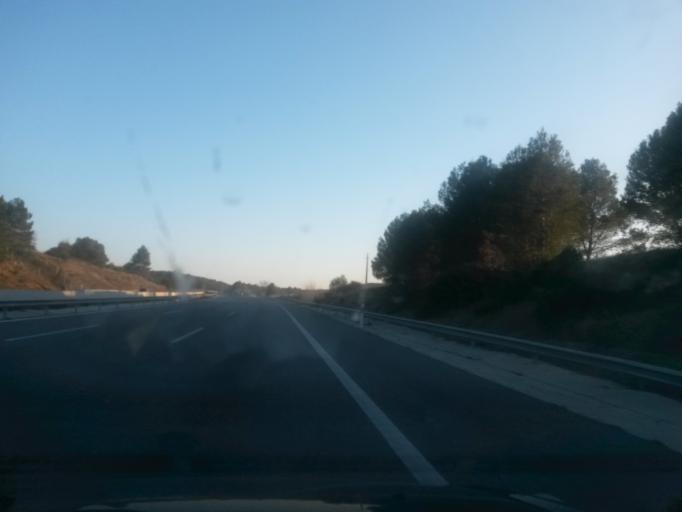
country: ES
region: Catalonia
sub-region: Provincia de Girona
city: Bascara
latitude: 42.1549
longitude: 2.9166
